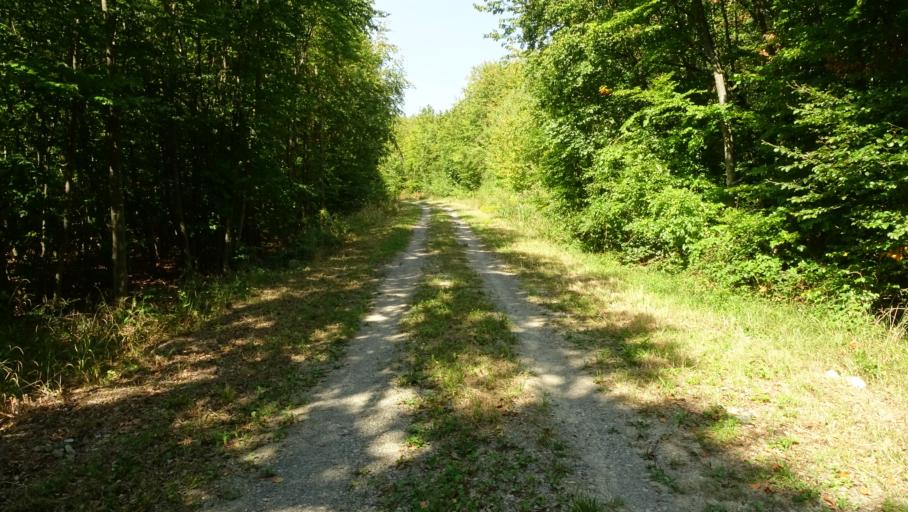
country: DE
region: Baden-Wuerttemberg
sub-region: Karlsruhe Region
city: Obrigheim
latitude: 49.3886
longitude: 9.1174
